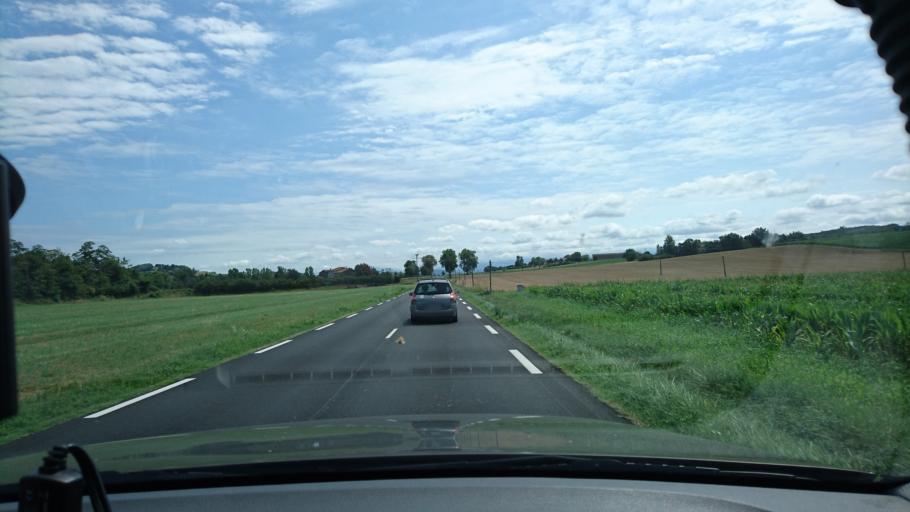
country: FR
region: Midi-Pyrenees
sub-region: Departement de l'Ariege
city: Lezat-sur-Leze
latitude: 43.1952
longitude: 1.3930
